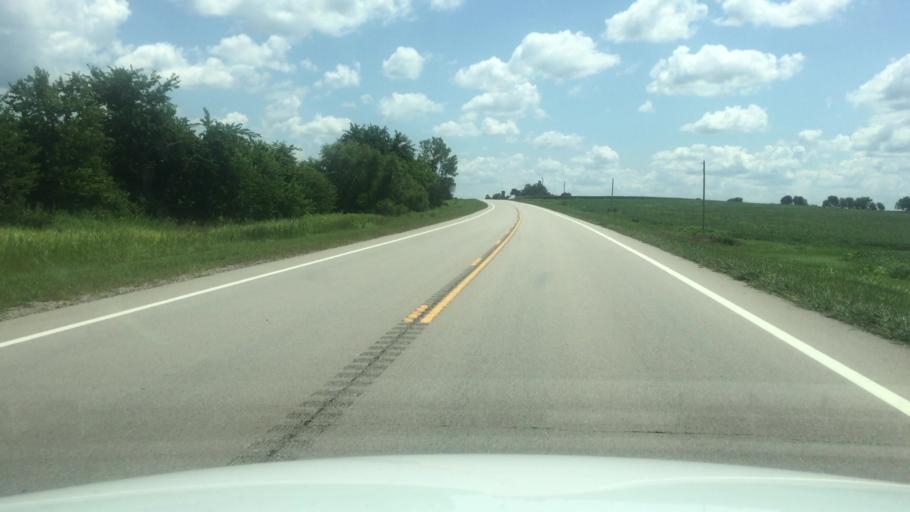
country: US
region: Kansas
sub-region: Brown County
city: Horton
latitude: 39.6127
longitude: -95.3462
